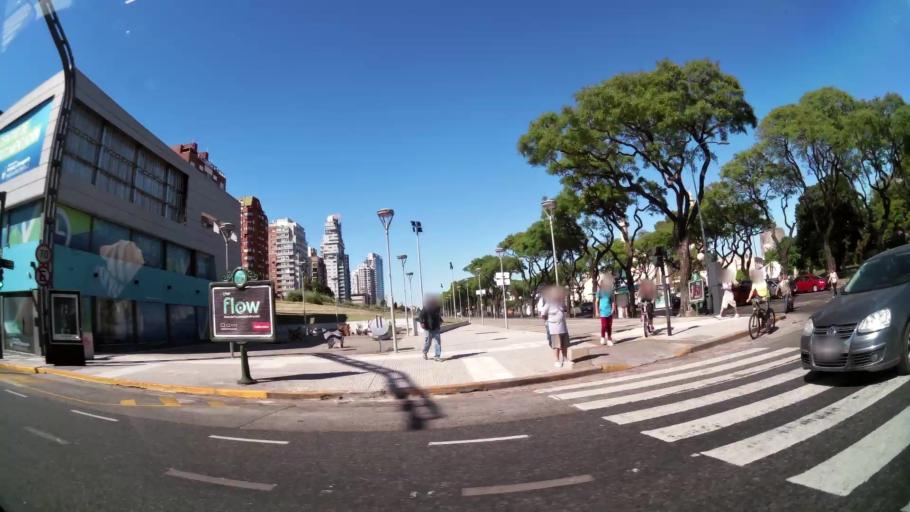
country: AR
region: Buenos Aires F.D.
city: Colegiales
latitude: -34.5714
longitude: -58.4231
